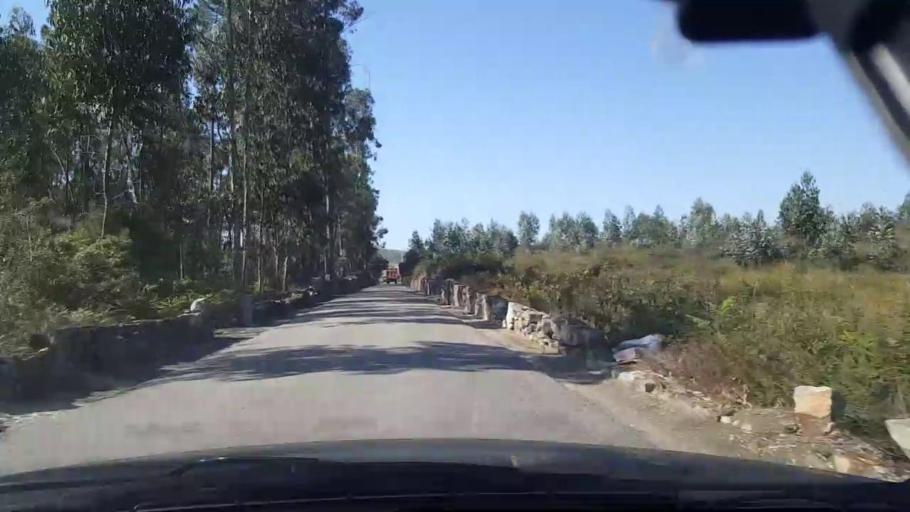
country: PT
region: Braga
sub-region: Vila Nova de Famalicao
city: Ribeirao
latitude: 41.3573
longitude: -8.6406
